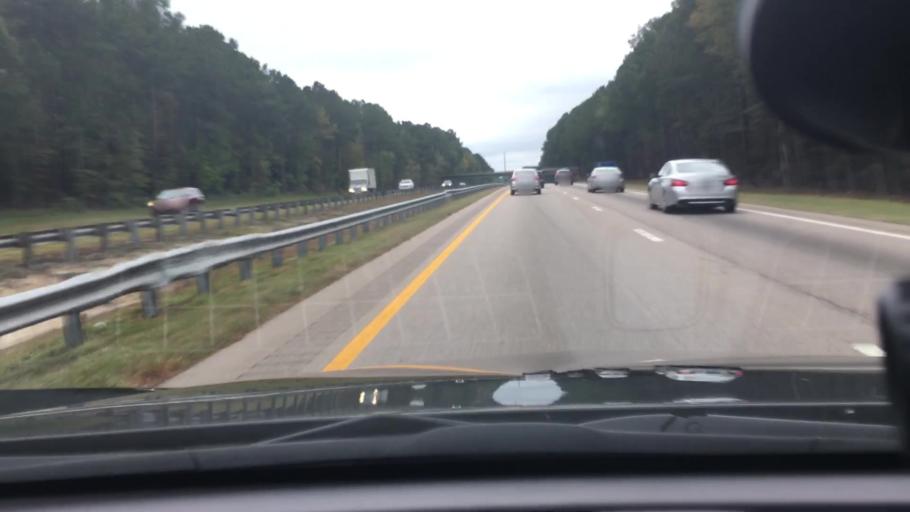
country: US
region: North Carolina
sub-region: Wake County
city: Wendell
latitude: 35.8183
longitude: -78.3959
